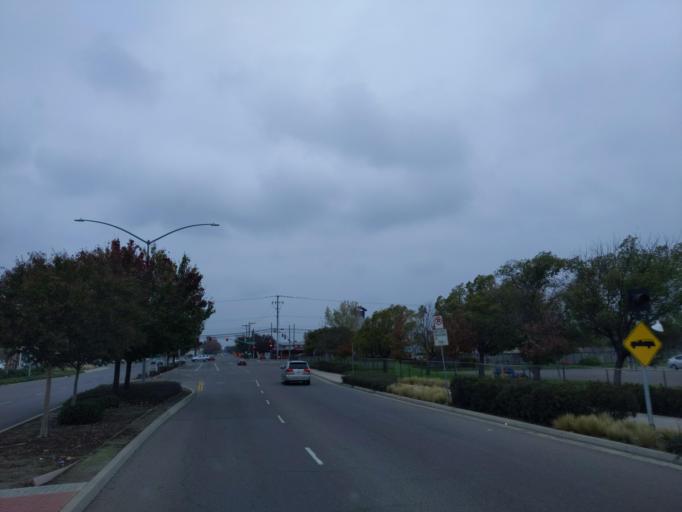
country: US
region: California
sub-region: San Joaquin County
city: Kennedy
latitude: 37.9401
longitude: -121.2700
